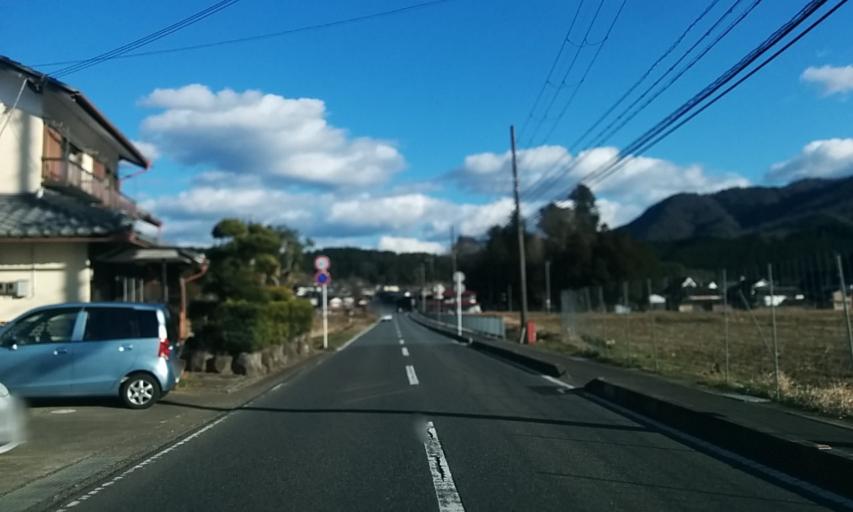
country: JP
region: Kyoto
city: Fukuchiyama
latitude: 35.2863
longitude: 135.0636
